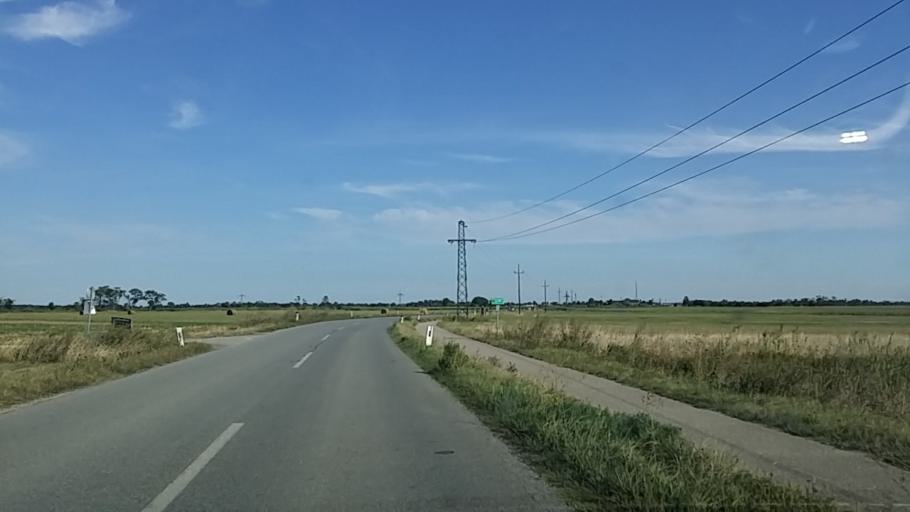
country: AT
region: Burgenland
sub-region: Politischer Bezirk Neusiedl am See
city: Apetlon
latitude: 47.7266
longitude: 16.8610
